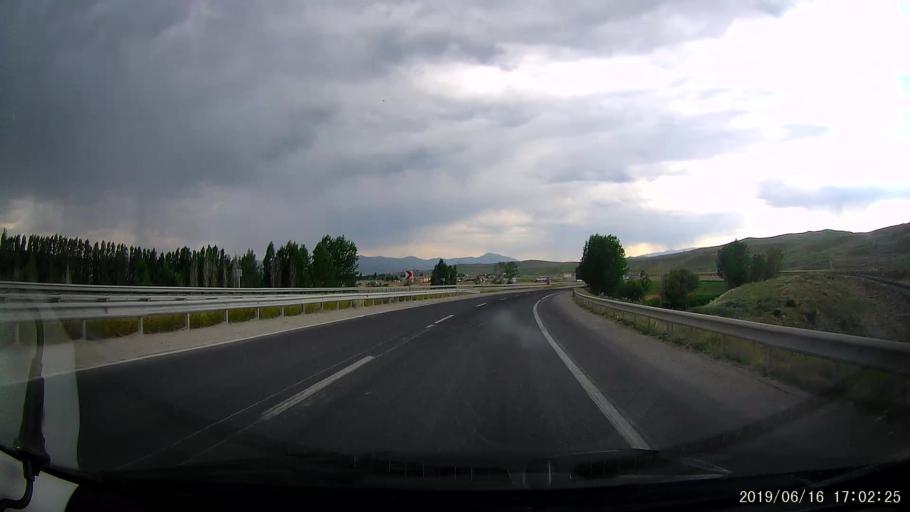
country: TR
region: Erzurum
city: Askale
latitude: 39.9403
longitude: 40.7547
